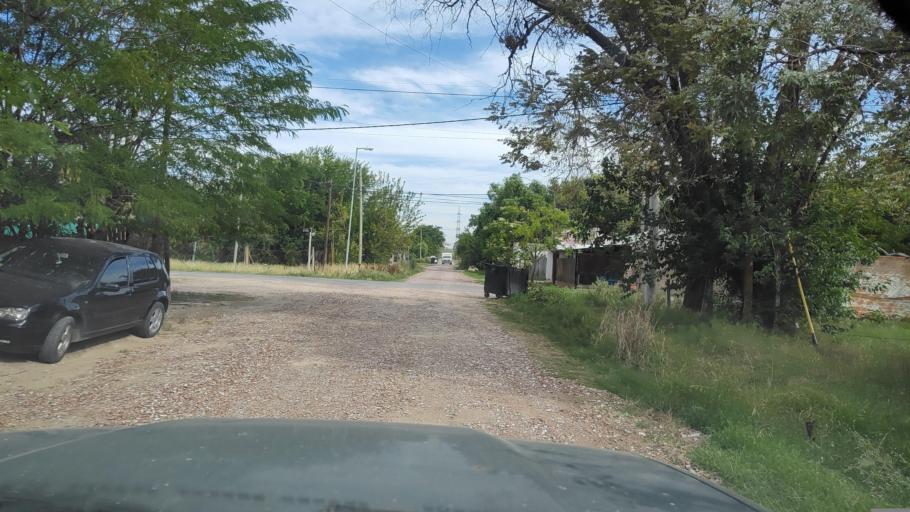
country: AR
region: Buenos Aires
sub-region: Partido de Lujan
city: Lujan
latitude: -34.5777
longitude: -59.0960
